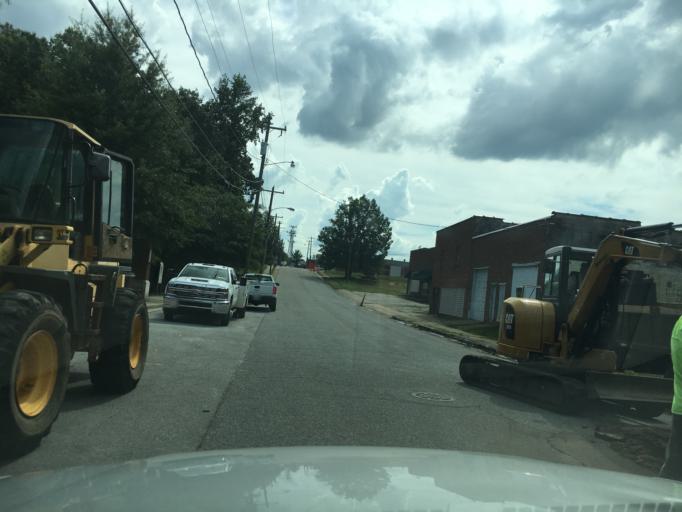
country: US
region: South Carolina
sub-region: Greenville County
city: Greer
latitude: 34.9403
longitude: -82.2237
